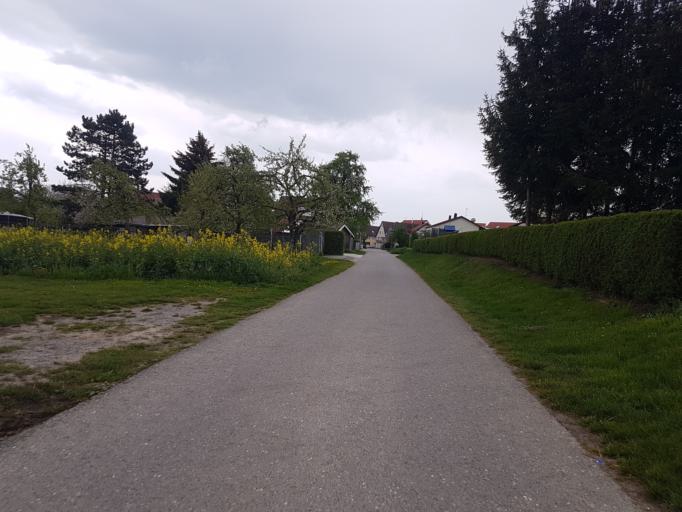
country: DE
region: Baden-Wuerttemberg
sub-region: Regierungsbezirk Stuttgart
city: Bondorf
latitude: 48.4982
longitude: 8.8066
